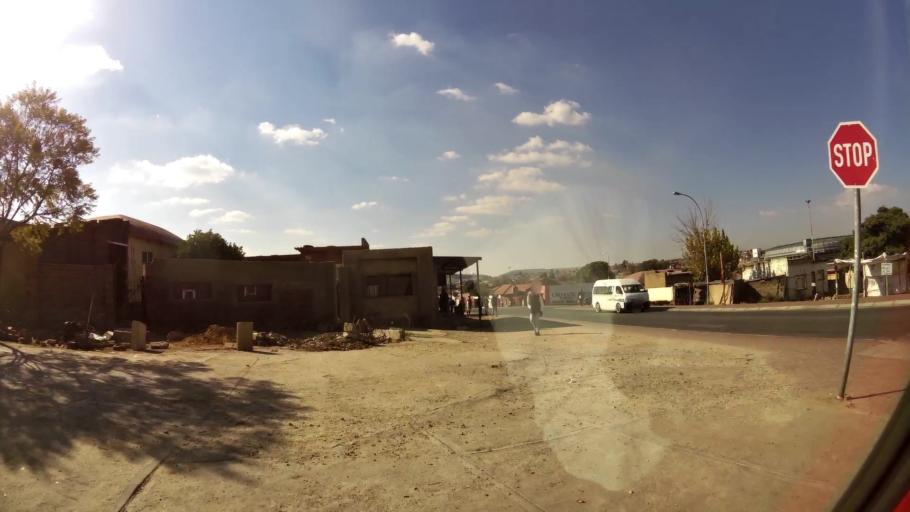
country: ZA
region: Gauteng
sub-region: City of Johannesburg Metropolitan Municipality
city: Soweto
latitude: -26.2268
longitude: 27.9185
